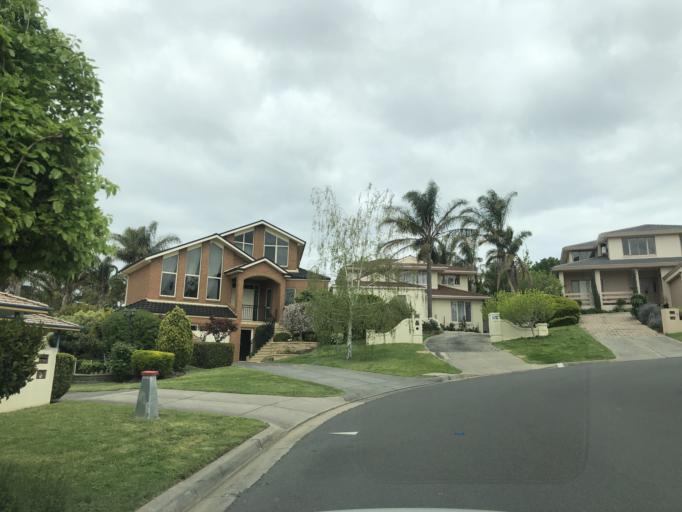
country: AU
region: Victoria
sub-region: Monash
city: Mulgrave
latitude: -37.9282
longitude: 145.1979
